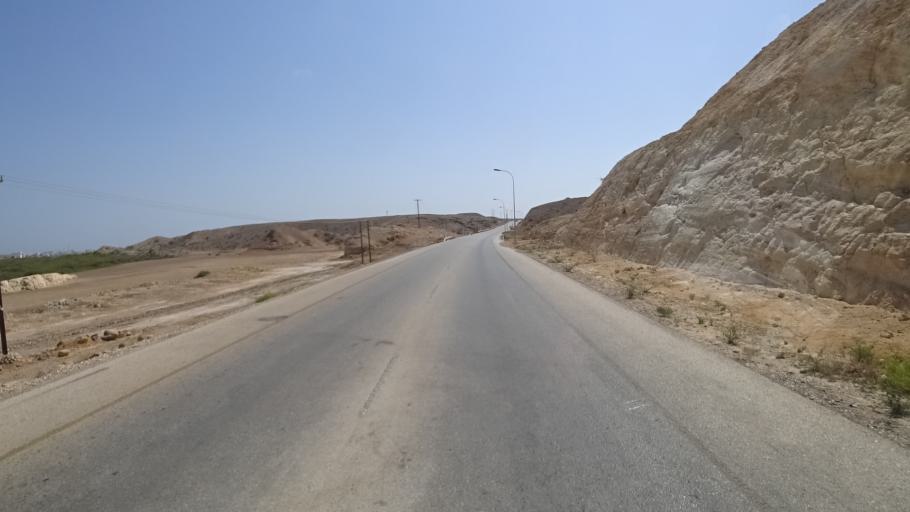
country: OM
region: Ash Sharqiyah
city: Sur
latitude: 22.5432
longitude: 59.5119
